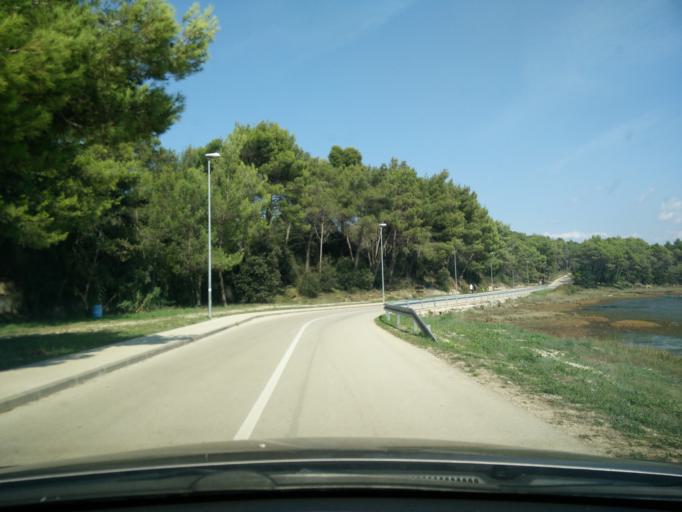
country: HR
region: Istarska
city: Novigrad
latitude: 45.2852
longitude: 13.5993
